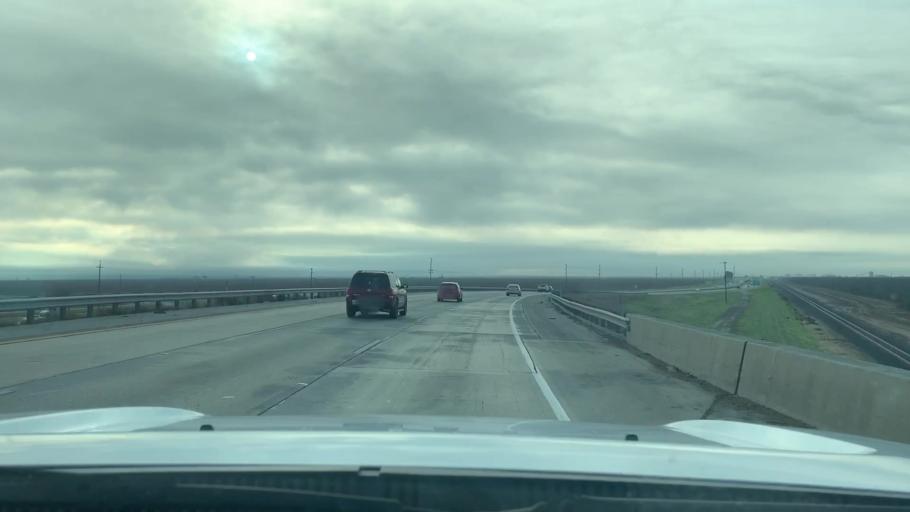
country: US
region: California
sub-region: Kern County
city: McFarland
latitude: 35.5903
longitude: -119.2058
